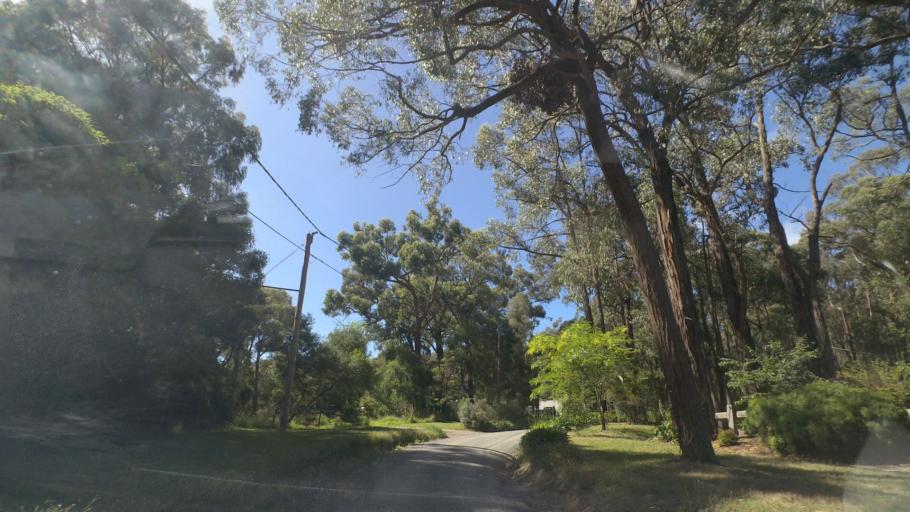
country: AU
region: Victoria
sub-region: Yarra Ranges
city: Kalorama
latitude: -37.8020
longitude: 145.3671
